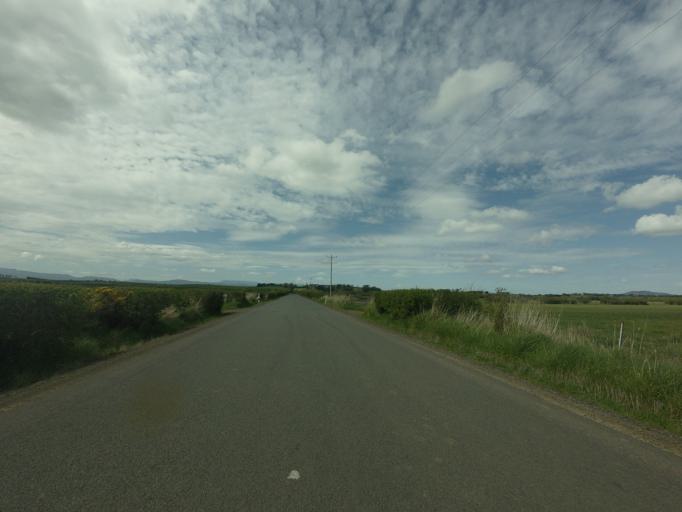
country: AU
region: Tasmania
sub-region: Northern Midlands
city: Longford
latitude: -41.6251
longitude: 147.1325
